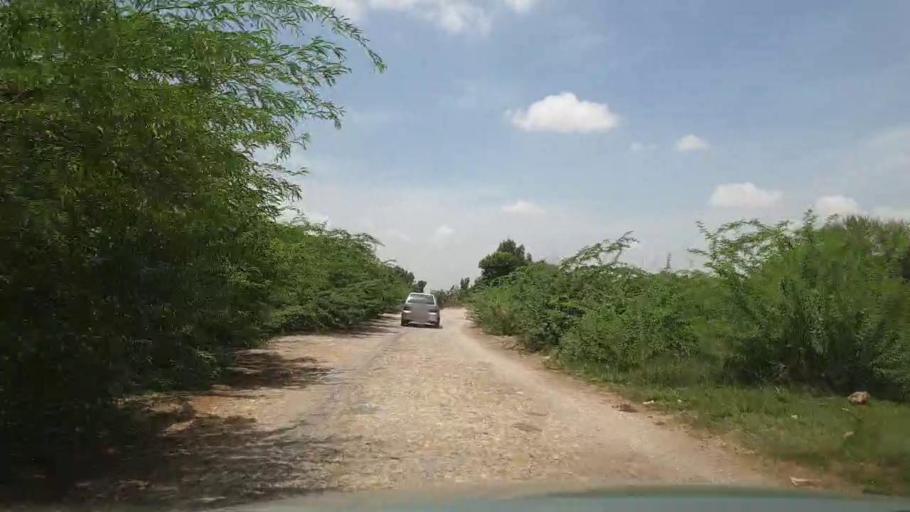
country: PK
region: Sindh
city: Kot Diji
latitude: 27.1547
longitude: 68.9762
